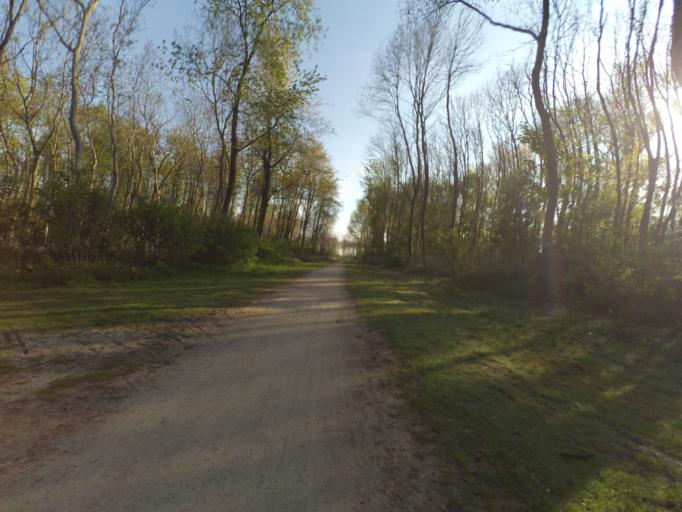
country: NL
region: Flevoland
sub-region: Gemeente Almere
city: Almere Stad
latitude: 52.3818
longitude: 5.2958
